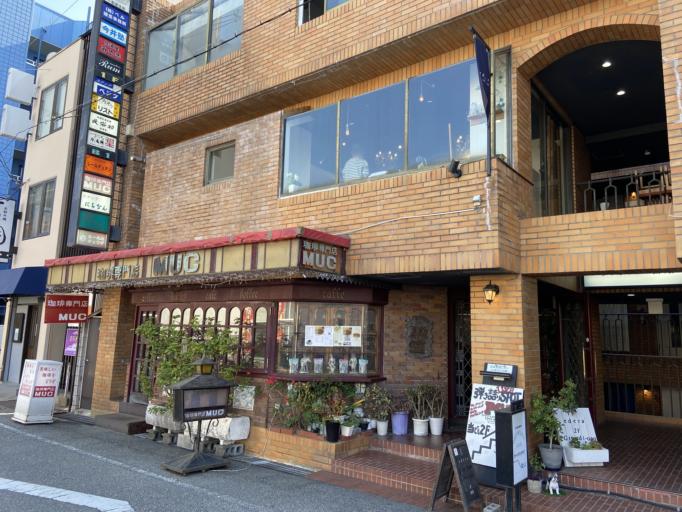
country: JP
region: Hyogo
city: Amagasaki
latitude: 34.7398
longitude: 135.3752
